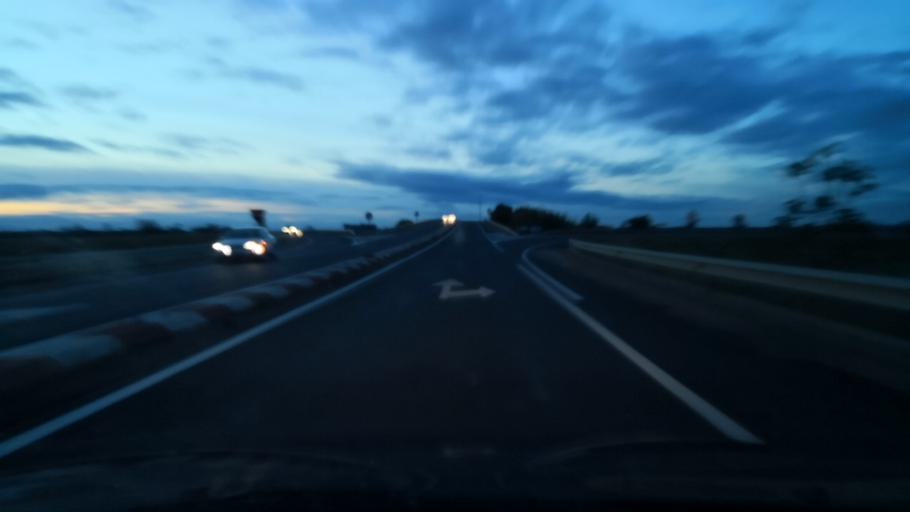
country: ES
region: Extremadura
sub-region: Provincia de Badajoz
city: Badajoz
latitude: 38.9182
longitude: -6.9627
